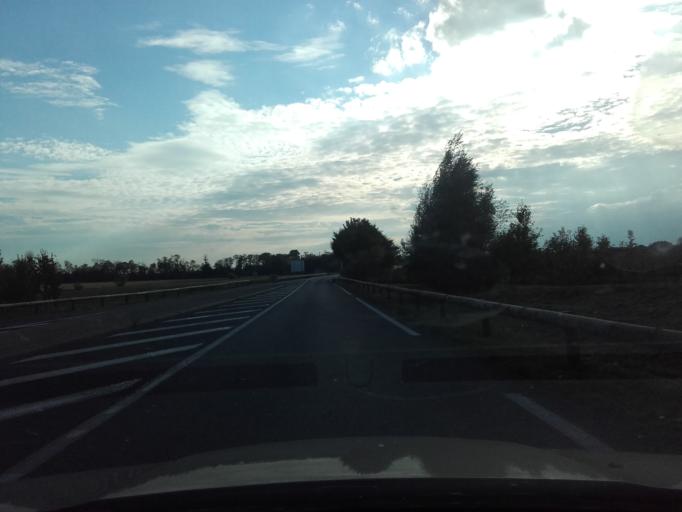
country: FR
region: Centre
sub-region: Departement d'Indre-et-Loire
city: Parcay-Meslay
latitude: 47.4633
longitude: 0.7436
